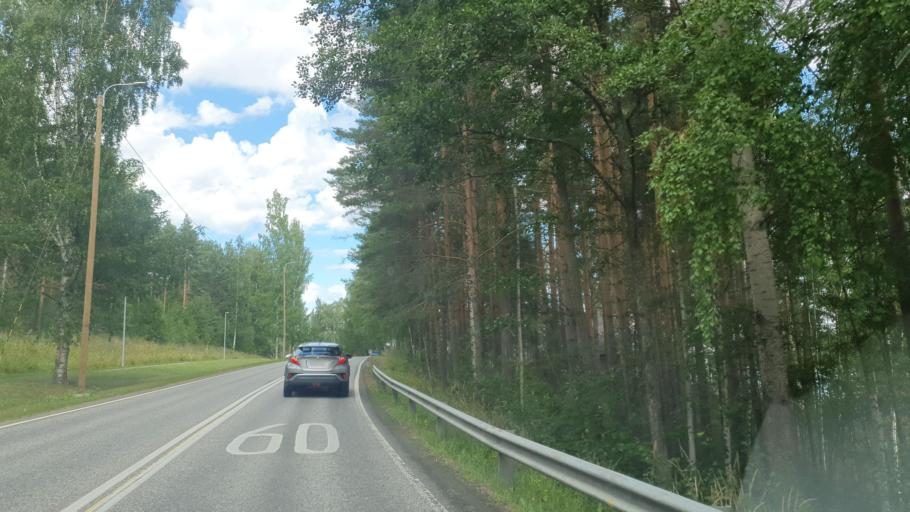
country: FI
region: Central Finland
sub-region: Jyvaeskylae
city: Saeynaetsalo
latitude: 62.1441
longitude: 25.7454
